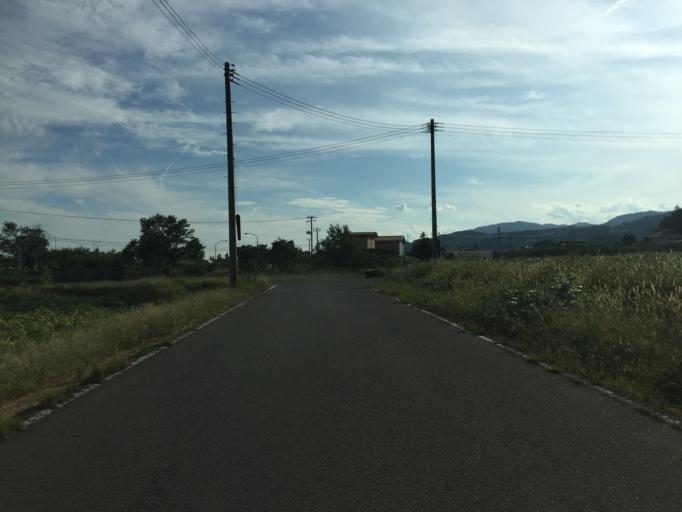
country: JP
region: Fukushima
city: Hobaramachi
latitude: 37.8817
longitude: 140.5298
